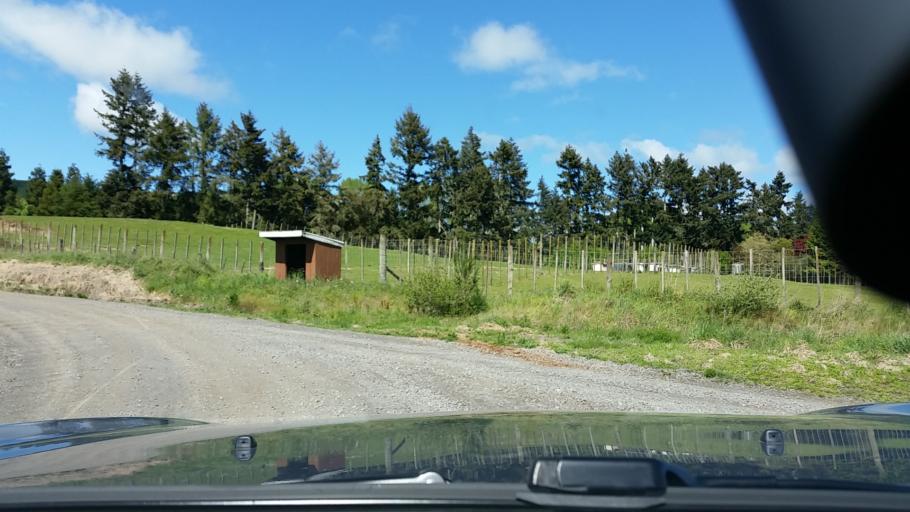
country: NZ
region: Bay of Plenty
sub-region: Rotorua District
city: Rotorua
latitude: -38.3528
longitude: 176.2317
